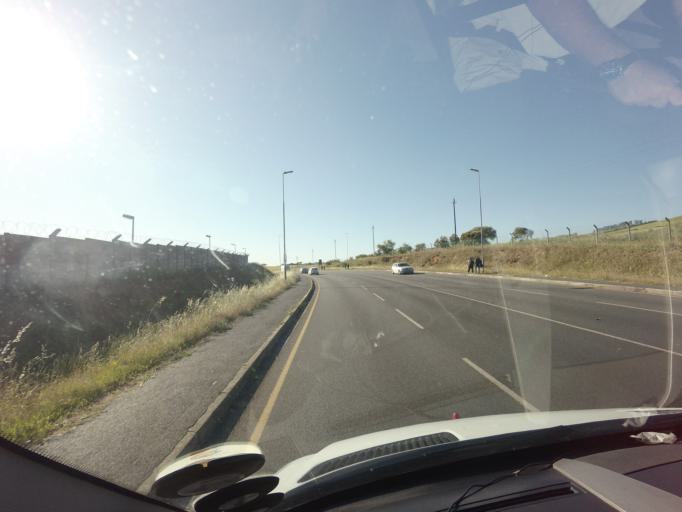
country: ZA
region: Western Cape
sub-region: Cape Winelands District Municipality
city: Stellenbosch
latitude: -33.9223
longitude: 18.8659
